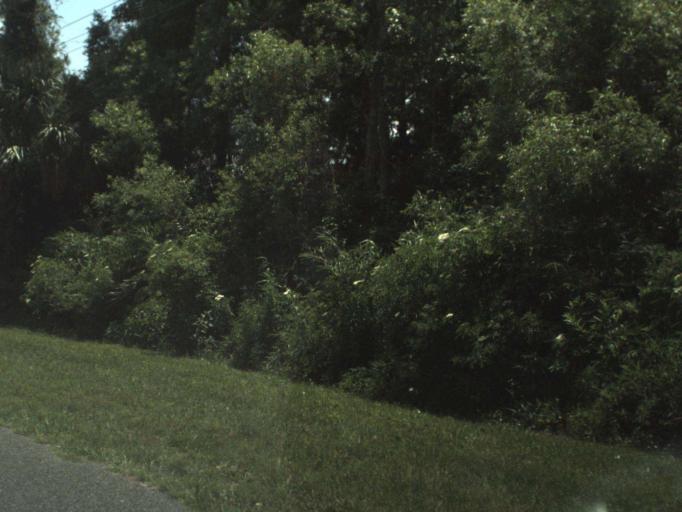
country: US
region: Florida
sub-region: Volusia County
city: Ormond-by-the-Sea
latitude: 29.3157
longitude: -81.1055
